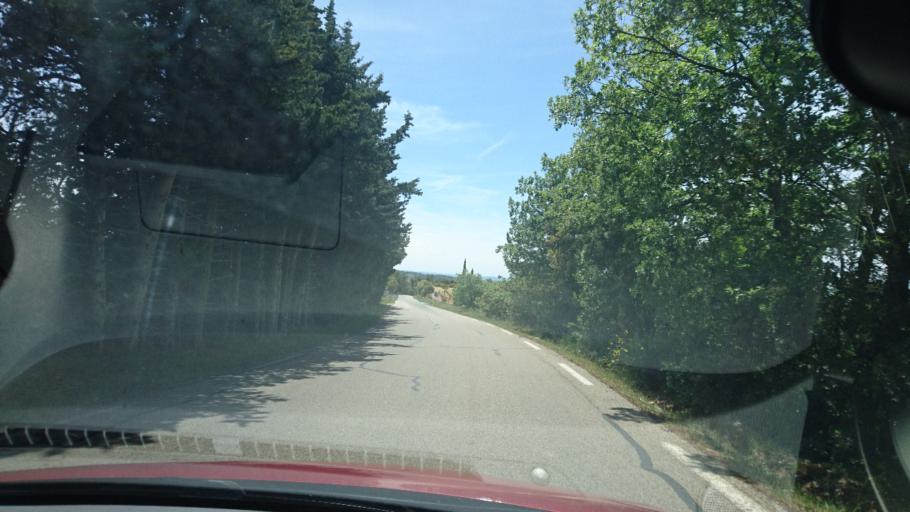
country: FR
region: Provence-Alpes-Cote d'Azur
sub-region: Departement du Vaucluse
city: Bedoin
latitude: 44.1221
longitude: 5.2144
